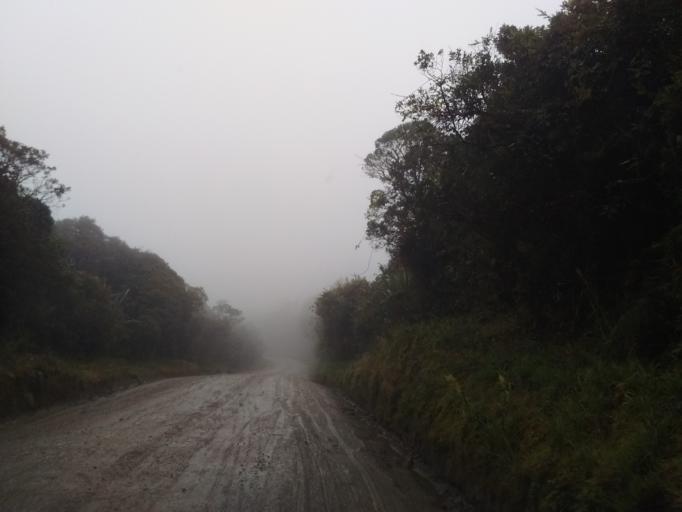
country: CO
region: Cauca
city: Paispamba
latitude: 2.1471
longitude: -76.4347
